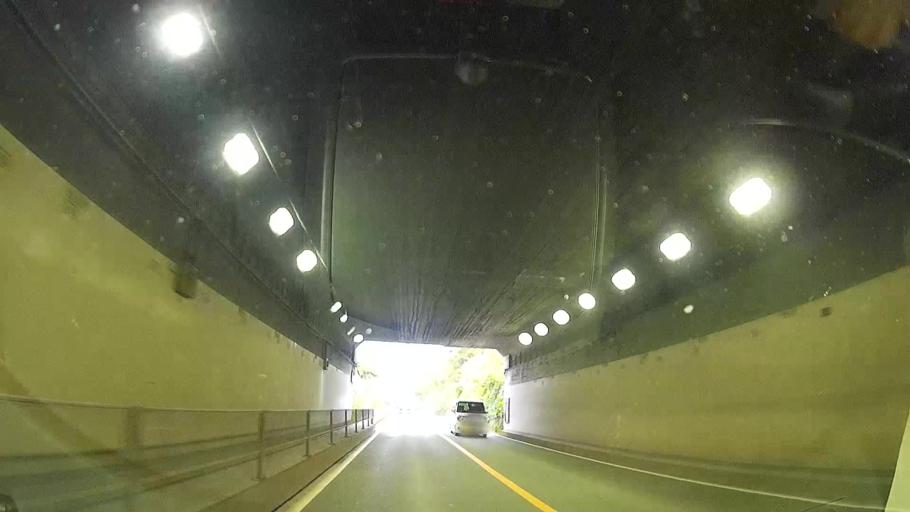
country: JP
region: Kumamoto
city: Ozu
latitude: 32.8382
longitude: 130.8533
